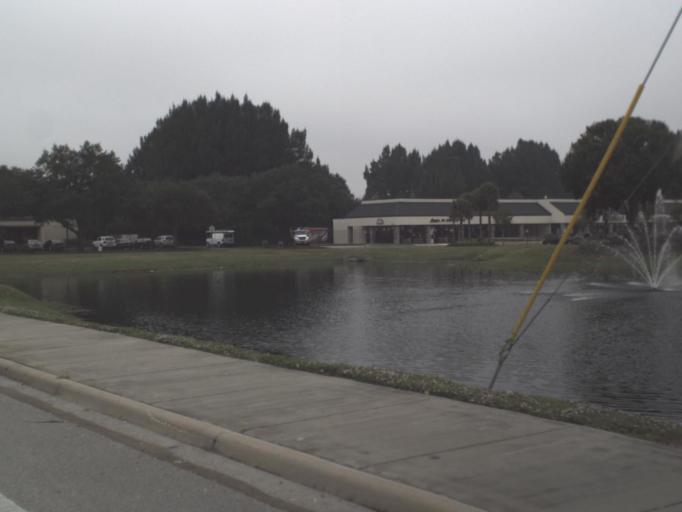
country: US
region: Florida
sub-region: Brevard County
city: Palm Bay
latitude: 27.9987
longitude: -80.6348
